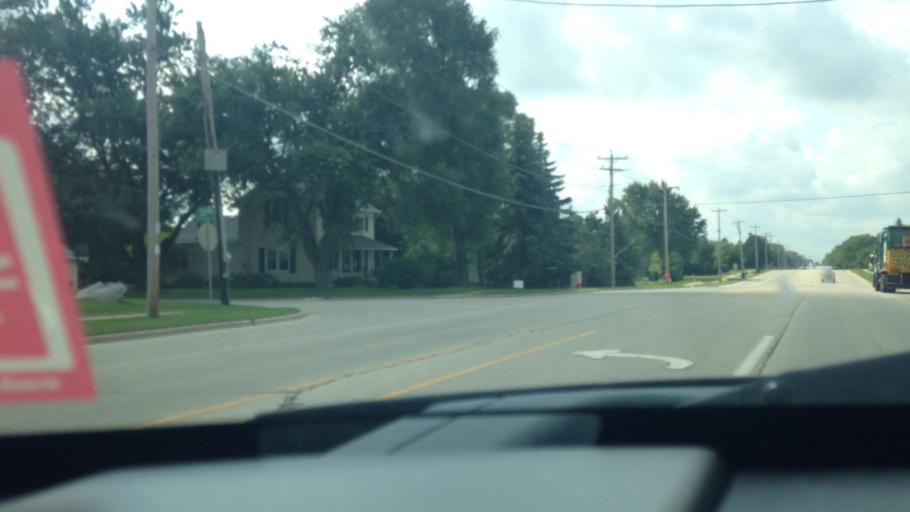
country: US
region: Wisconsin
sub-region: Waukesha County
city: Menomonee Falls
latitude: 43.1598
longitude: -88.1042
